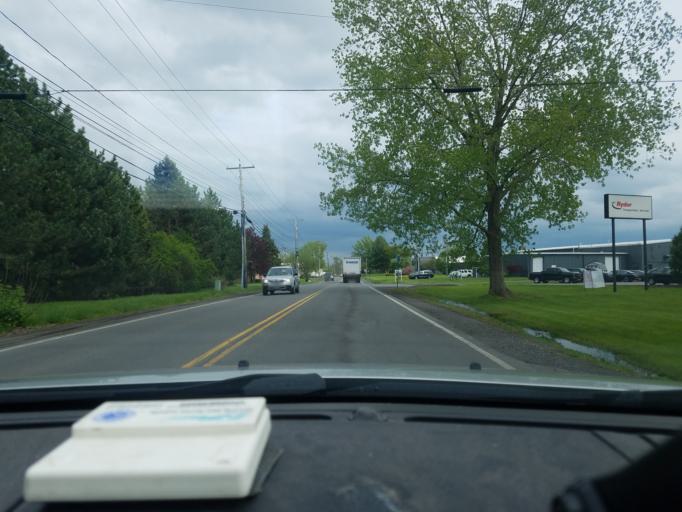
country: US
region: New York
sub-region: Onondaga County
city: Liverpool
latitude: 43.1139
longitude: -76.2028
